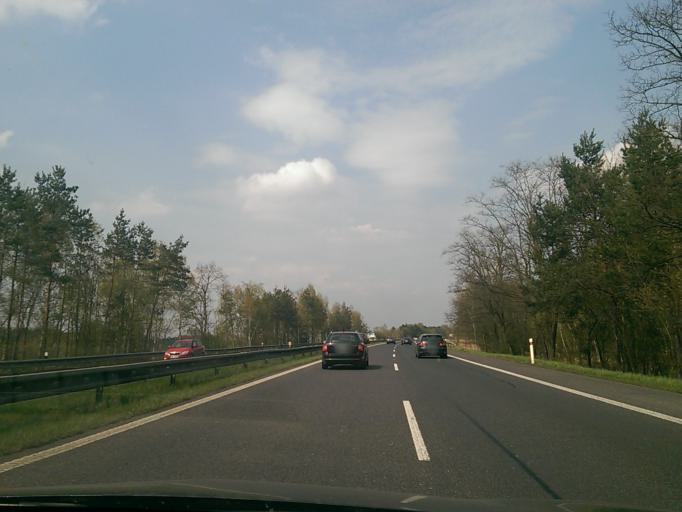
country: CZ
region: Central Bohemia
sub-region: Okres Mlada Boleslav
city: Mlada Boleslav
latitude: 50.3540
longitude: 14.8720
